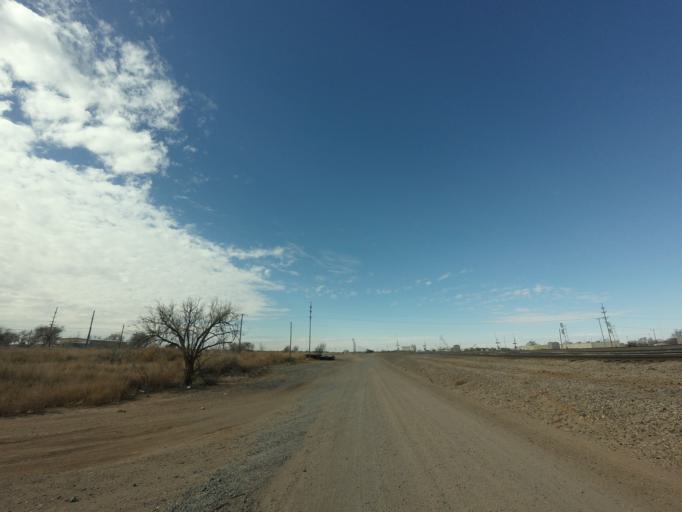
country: US
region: New Mexico
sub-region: Curry County
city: Clovis
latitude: 34.3985
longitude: -103.2304
